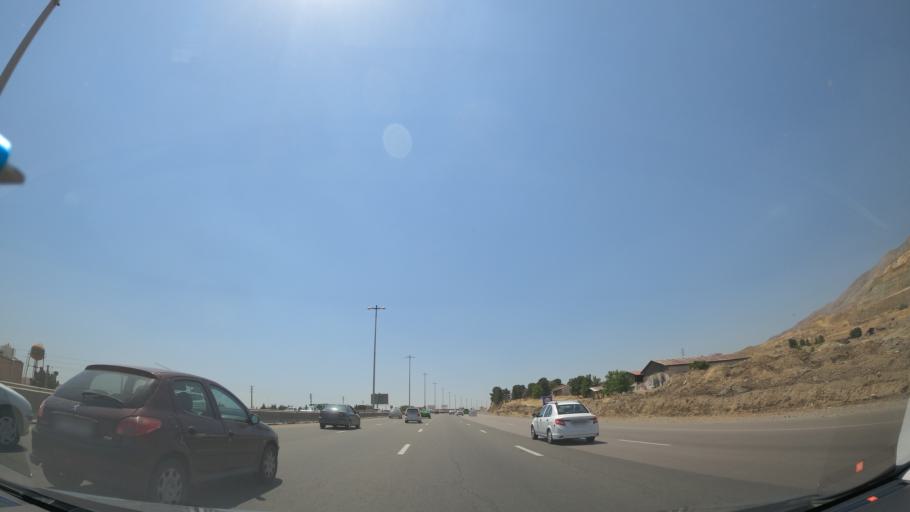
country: IR
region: Tehran
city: Shahr-e Qods
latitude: 35.7443
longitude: 51.0966
